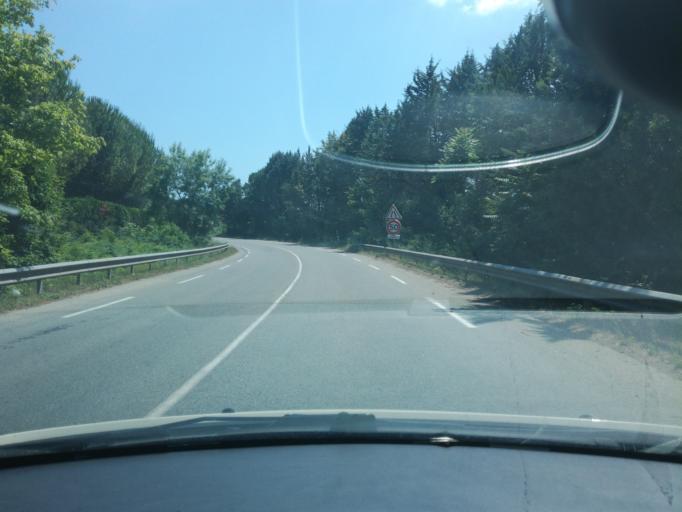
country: FR
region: Provence-Alpes-Cote d'Azur
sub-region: Departement du Var
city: Le Muy
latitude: 43.4811
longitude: 6.5653
